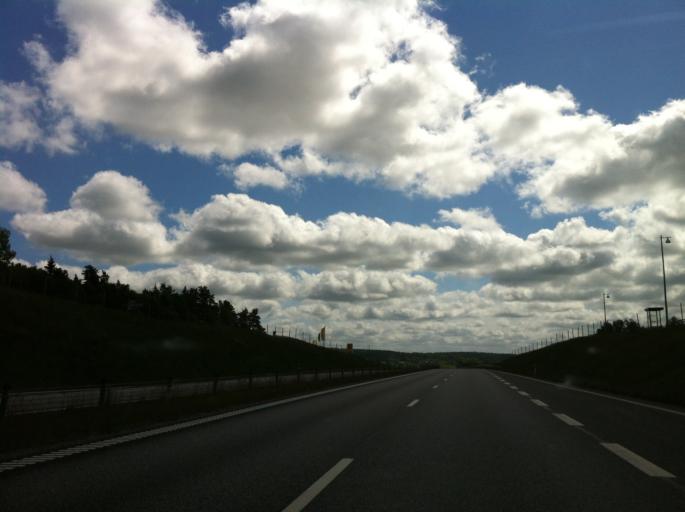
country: SE
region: Vaestra Goetaland
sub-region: Ale Kommun
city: Skepplanda
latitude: 57.9898
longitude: 12.1626
